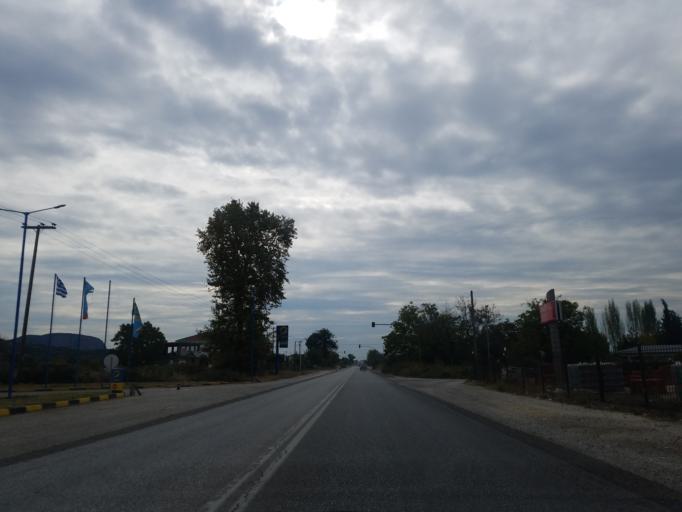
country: GR
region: Thessaly
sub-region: Trikala
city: Kalampaka
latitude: 39.6923
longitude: 21.6438
